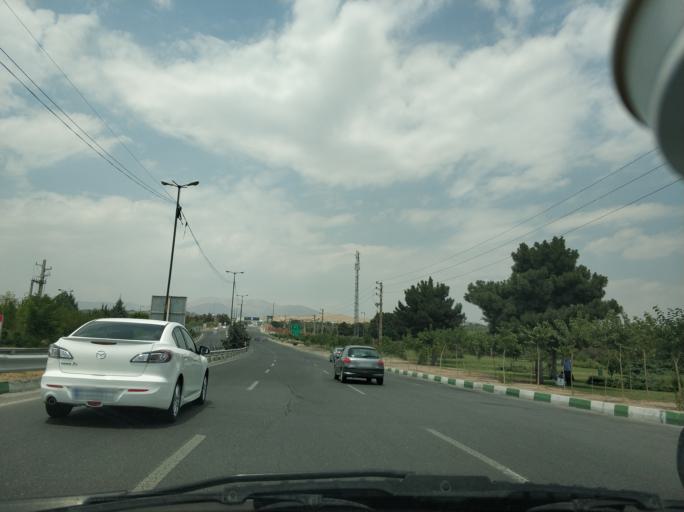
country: IR
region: Tehran
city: Tajrish
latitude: 35.7708
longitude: 51.5578
